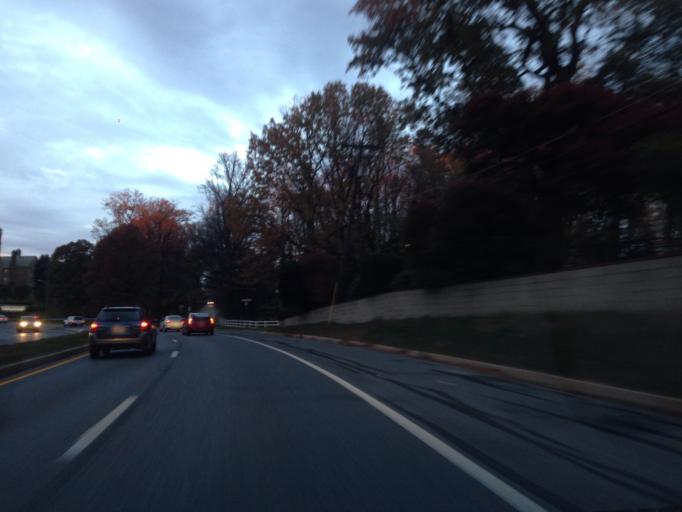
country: US
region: Maryland
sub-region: Baltimore County
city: Lutherville
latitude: 39.3986
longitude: -76.6260
